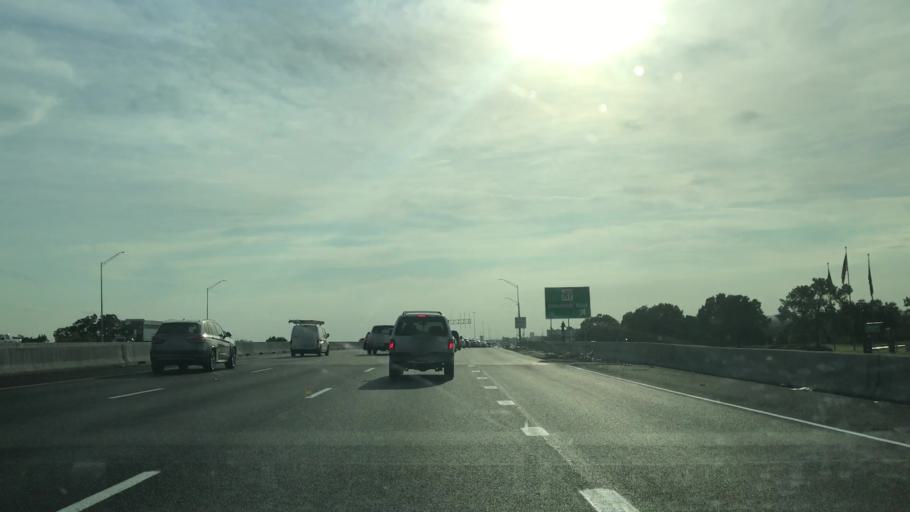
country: US
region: Texas
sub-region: Tarrant County
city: Euless
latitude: 32.8383
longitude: -97.0896
